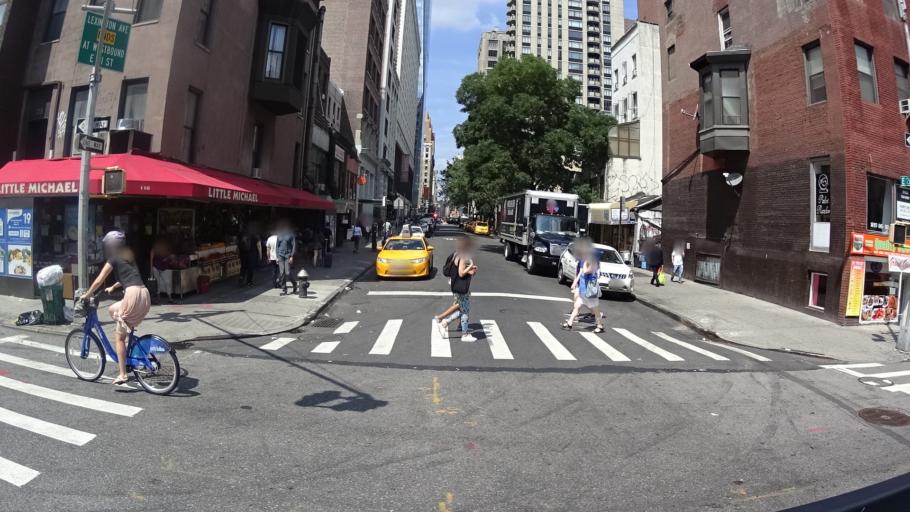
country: US
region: New York
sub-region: Queens County
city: Long Island City
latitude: 40.7427
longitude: -73.9824
